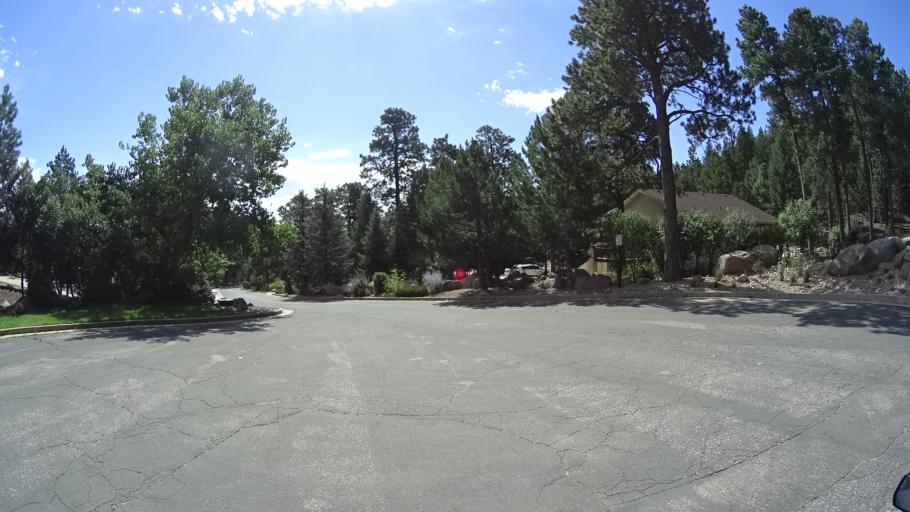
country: US
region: Colorado
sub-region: El Paso County
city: Fort Carson
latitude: 38.7541
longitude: -104.8413
